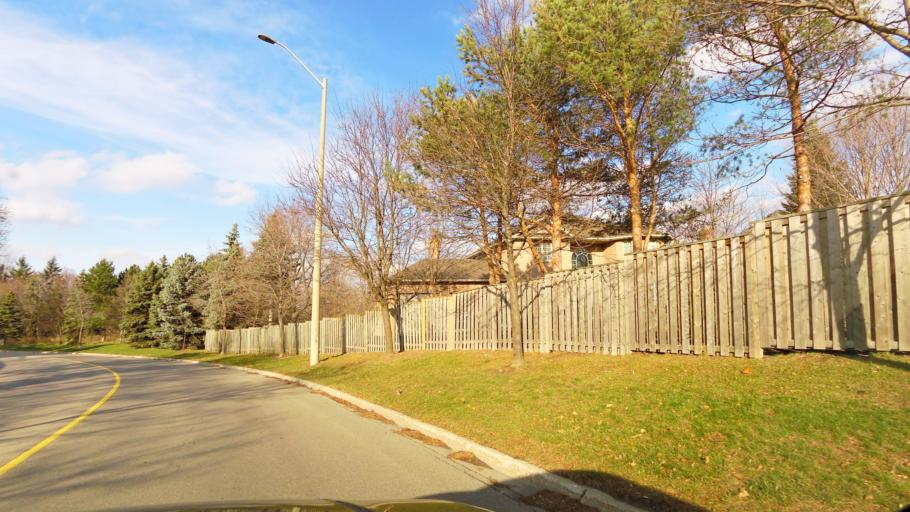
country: CA
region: Ontario
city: Mississauga
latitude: 43.5316
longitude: -79.6515
